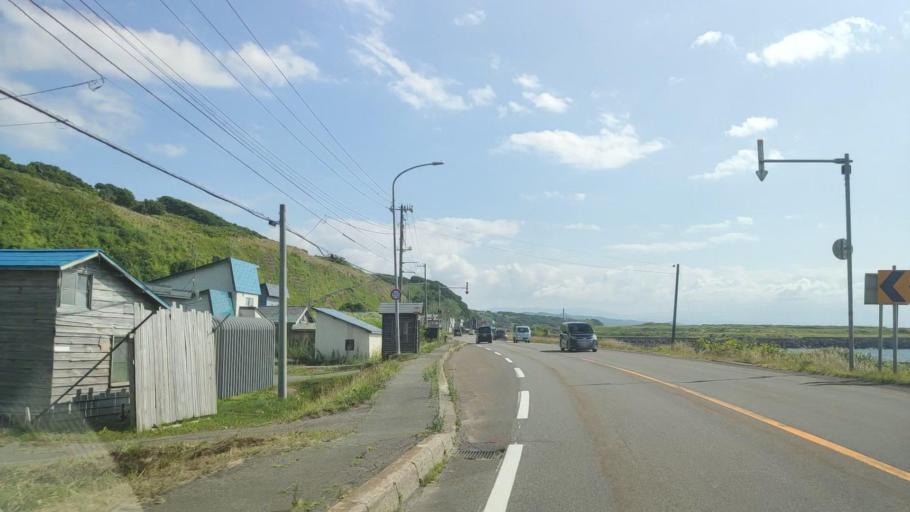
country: JP
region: Hokkaido
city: Rumoi
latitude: 43.9790
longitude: 141.6464
